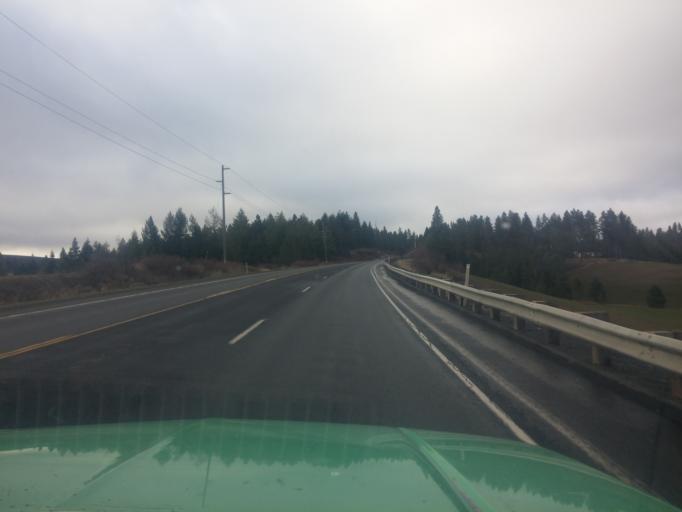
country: US
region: Idaho
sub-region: Latah County
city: Moscow
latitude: 46.8801
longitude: -117.0035
